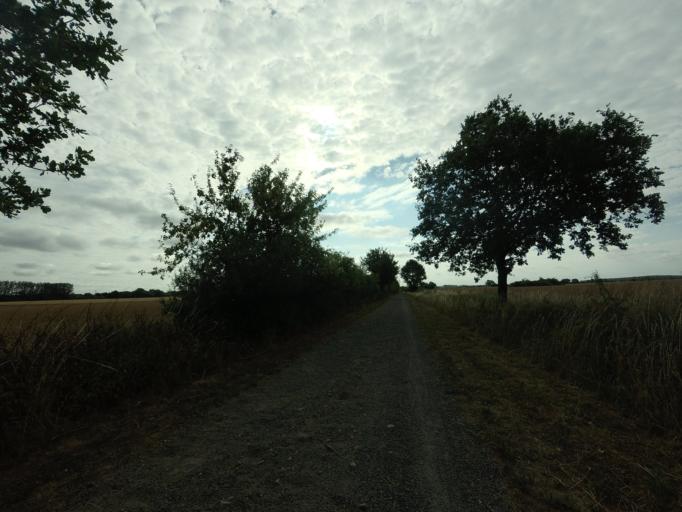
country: SE
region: Skane
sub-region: Helsingborg
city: Odakra
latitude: 56.1700
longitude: 12.7130
